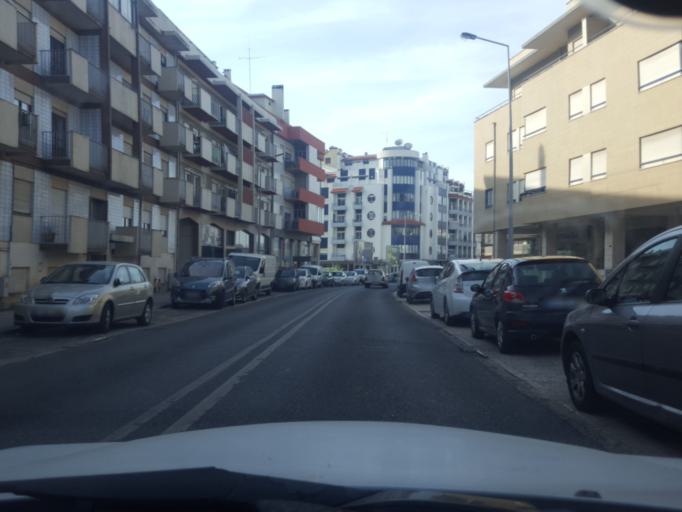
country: PT
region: Leiria
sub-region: Leiria
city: Leiria
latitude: 39.7387
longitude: -8.8020
